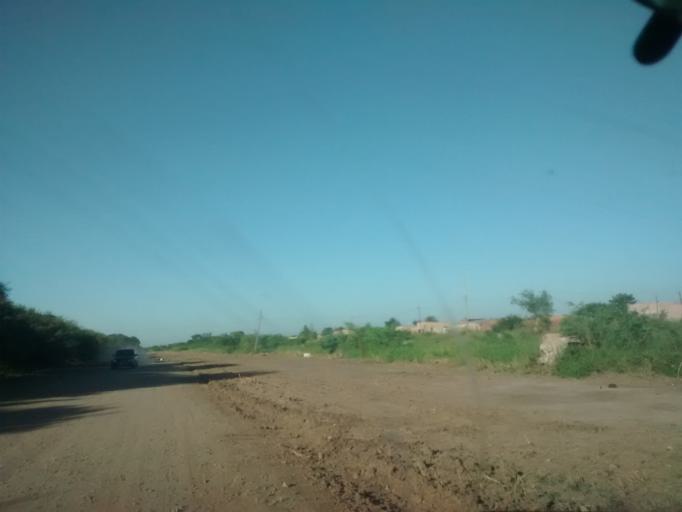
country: AR
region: Chaco
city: Resistencia
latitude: -27.4646
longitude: -59.0301
